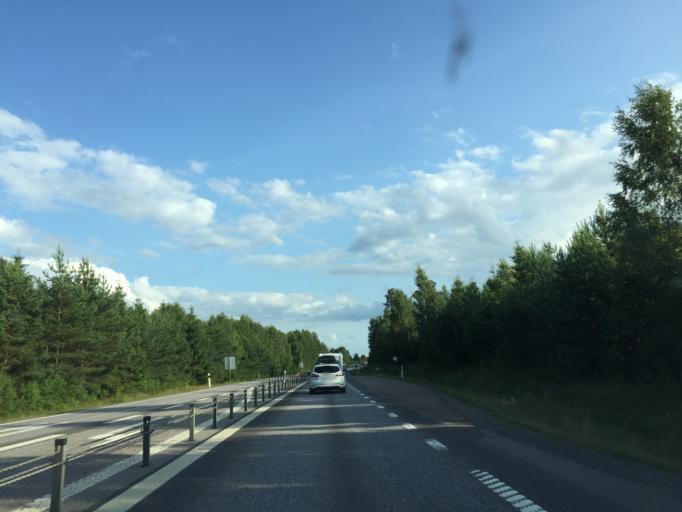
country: SE
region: OEstergoetland
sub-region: Motala Kommun
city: Motala
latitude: 58.5959
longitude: 14.9884
